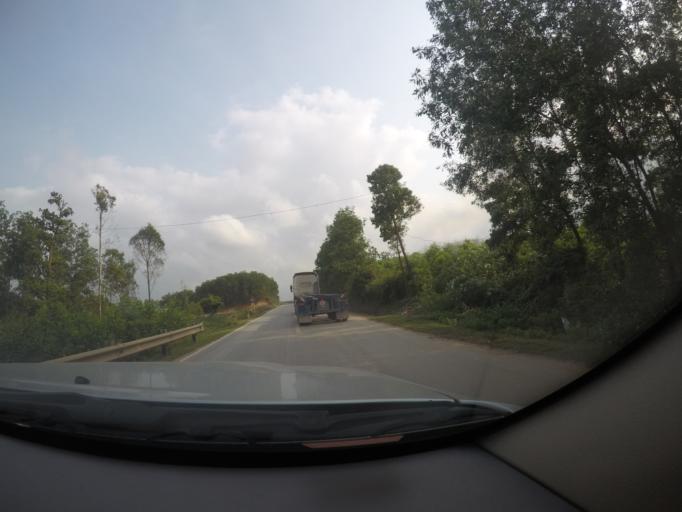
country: VN
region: Quang Binh
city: Kien Giang
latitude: 17.1035
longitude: 106.8461
